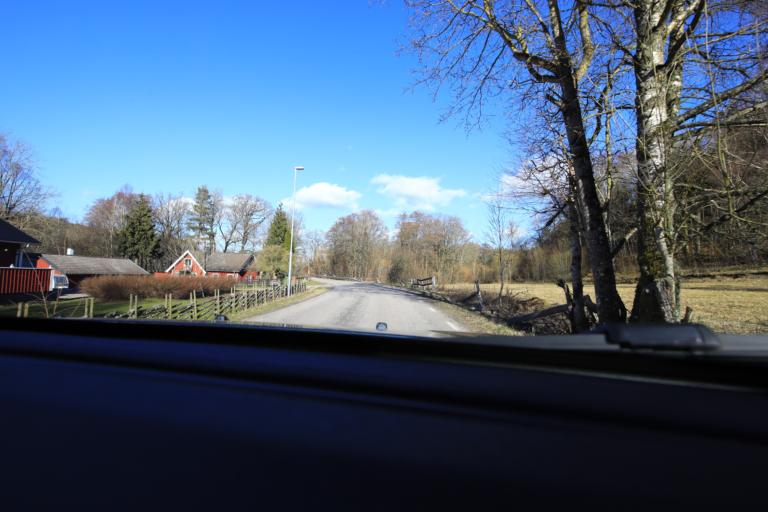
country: SE
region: Halland
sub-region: Varbergs Kommun
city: Tvaaker
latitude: 57.0646
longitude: 12.4854
